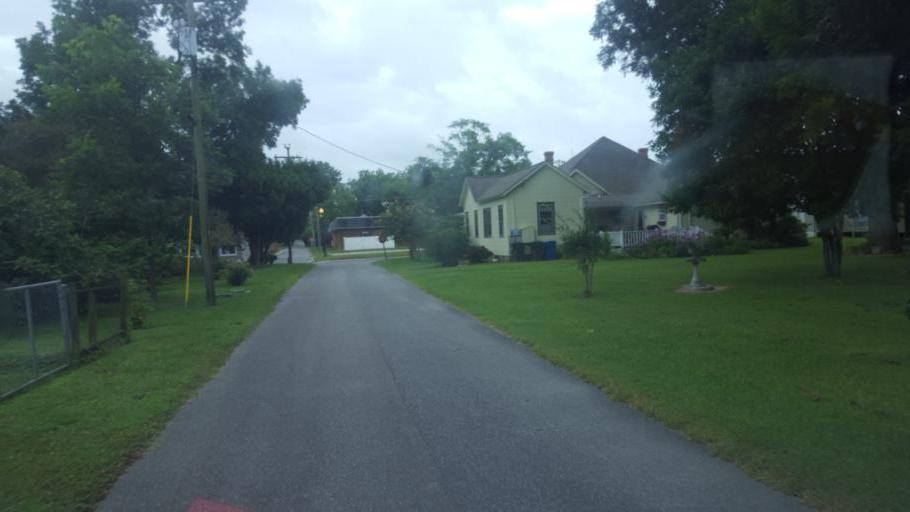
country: US
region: North Carolina
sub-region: Tyrrell County
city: Columbia
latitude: 35.9193
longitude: -76.2512
